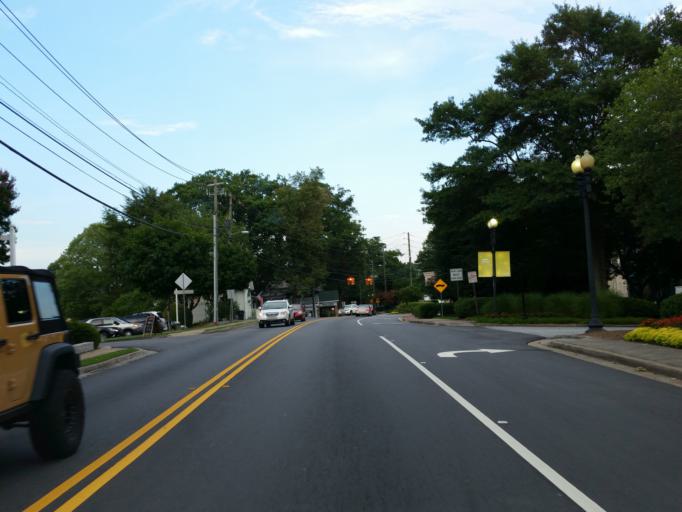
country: US
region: Georgia
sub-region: Cobb County
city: Vinings
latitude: 33.8662
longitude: -84.4673
